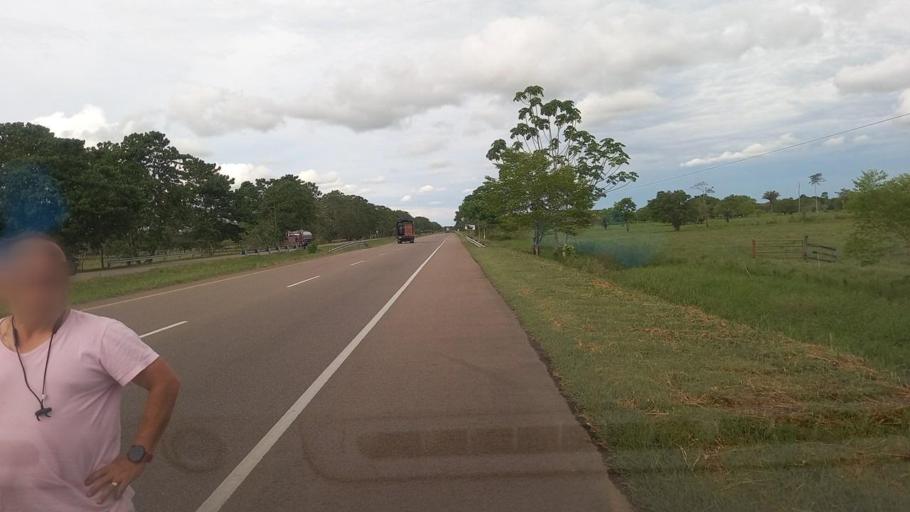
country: CO
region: Antioquia
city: Puerto Berrio
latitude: 6.3897
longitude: -74.3699
